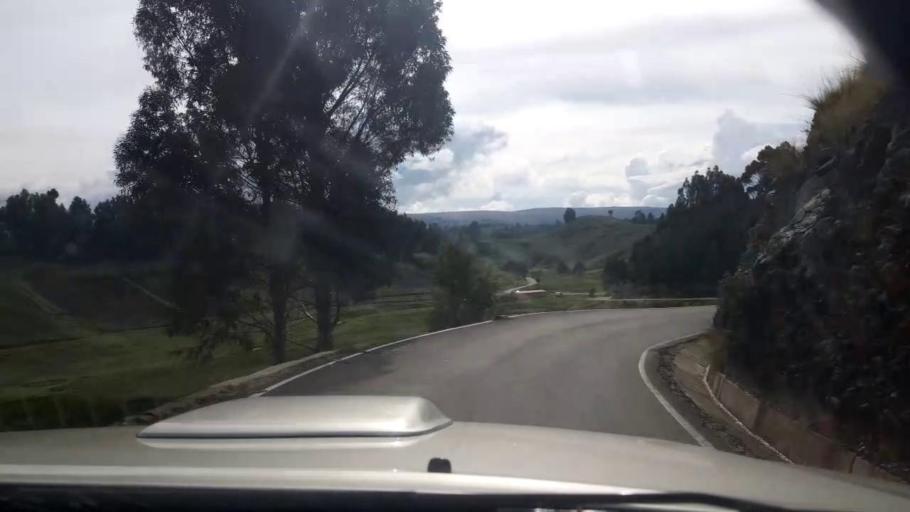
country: PE
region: Ayacucho
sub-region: Provincia de Cangallo
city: Pampa Cangallo
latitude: -13.4507
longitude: -74.2013
